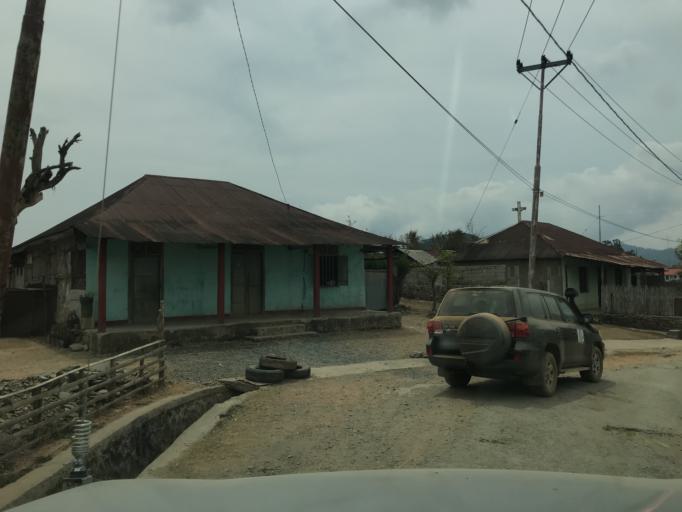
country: TL
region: Ermera
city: Gleno
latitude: -8.8364
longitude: 125.4283
